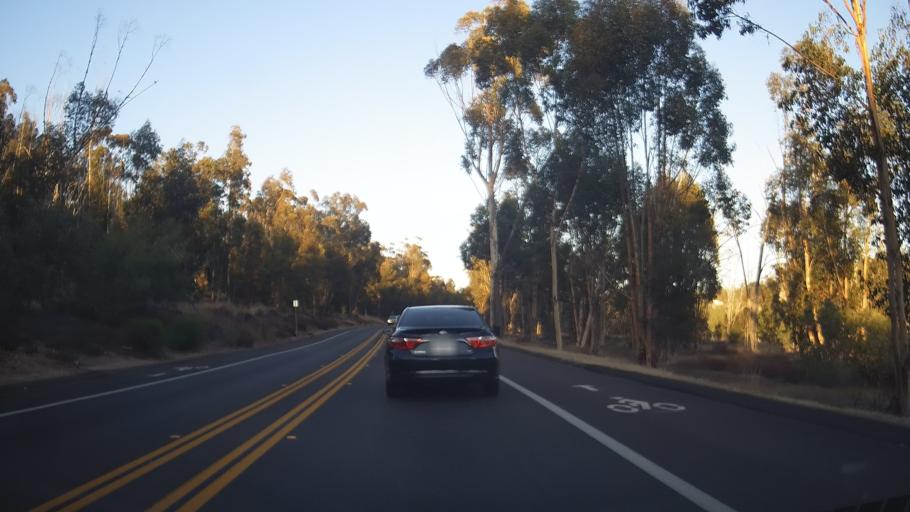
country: US
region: California
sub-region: San Diego County
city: Poway
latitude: 32.9004
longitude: -117.0969
